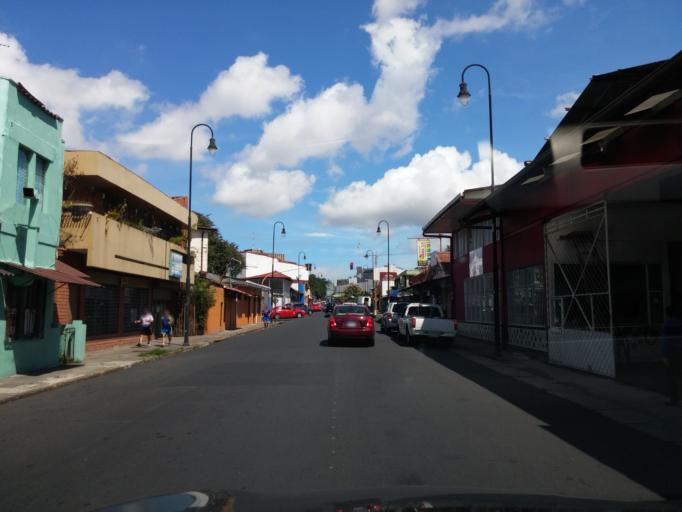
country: CR
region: San Jose
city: San Jose
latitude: 9.9267
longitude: -84.0726
